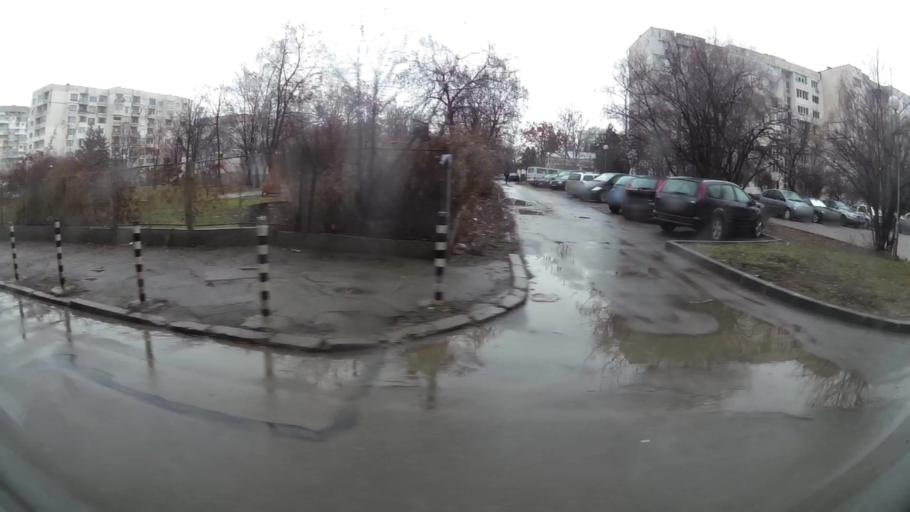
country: BG
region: Sofia-Capital
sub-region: Stolichna Obshtina
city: Sofia
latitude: 42.6429
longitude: 23.3760
